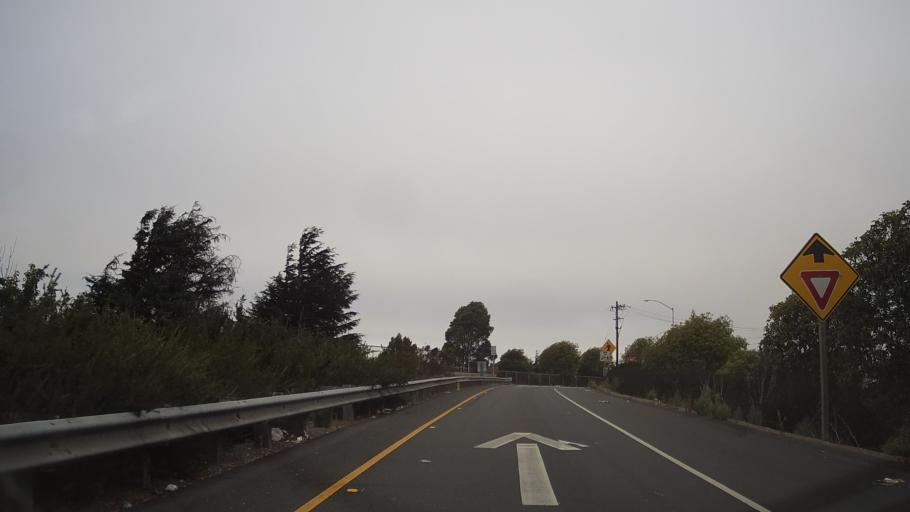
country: US
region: California
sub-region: Contra Costa County
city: Richmond
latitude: 37.9236
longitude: -122.3591
